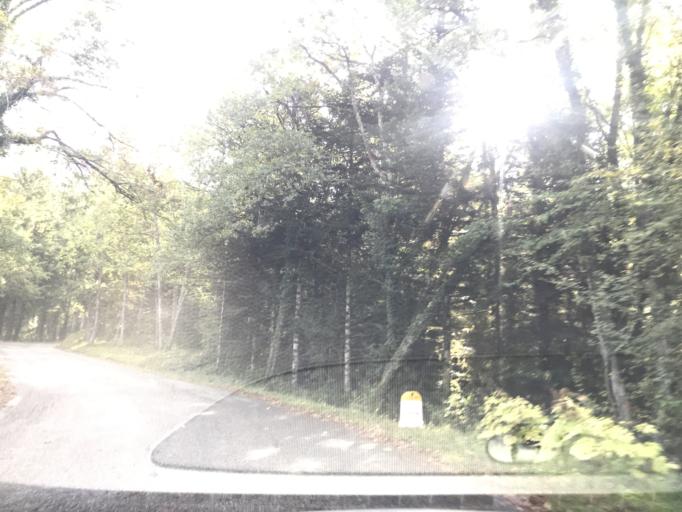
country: FR
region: Rhone-Alpes
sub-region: Departement de la Savoie
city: Novalaise
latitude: 45.6449
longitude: 5.7920
